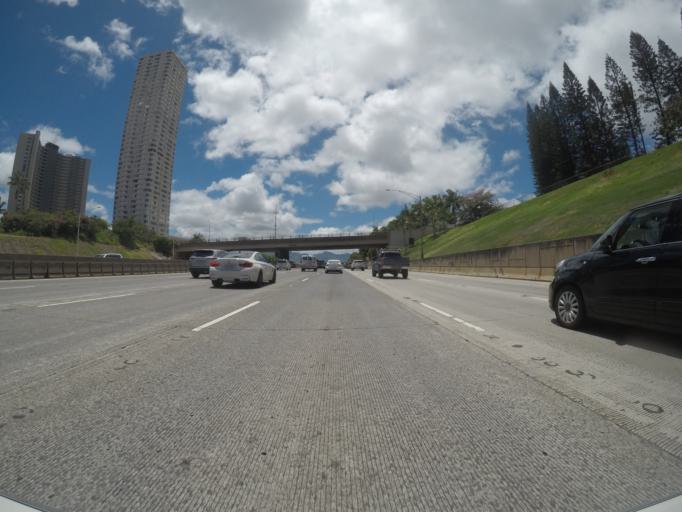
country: US
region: Hawaii
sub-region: Honolulu County
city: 'Aiea
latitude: 21.3885
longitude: -157.9402
